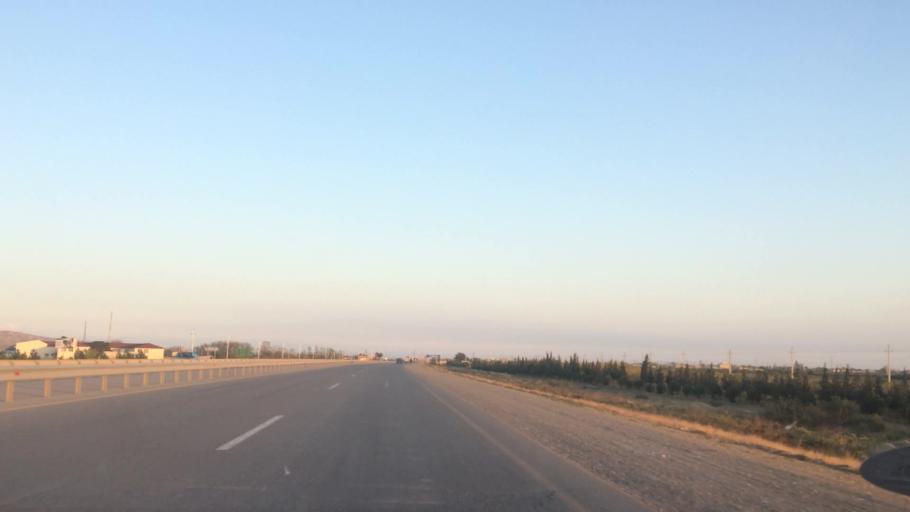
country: AZ
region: Baki
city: Qobustan
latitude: 39.9766
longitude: 49.2470
